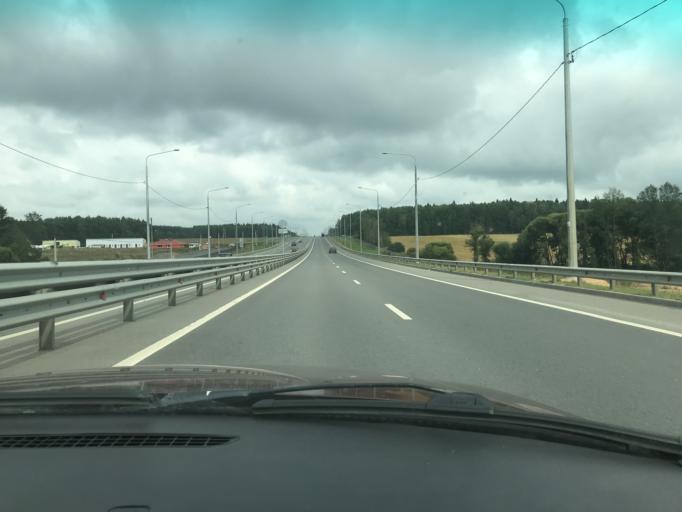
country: RU
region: Kaluga
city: Detchino
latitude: 54.8757
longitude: 36.3524
